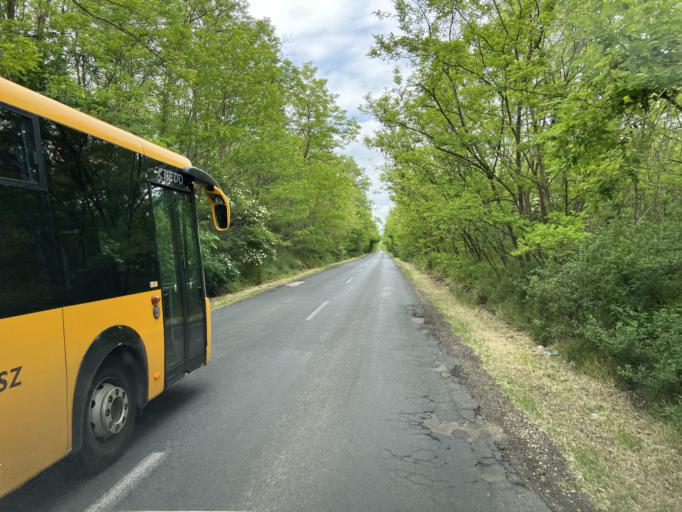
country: HU
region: Pest
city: Isaszeg
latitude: 47.5153
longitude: 19.4494
